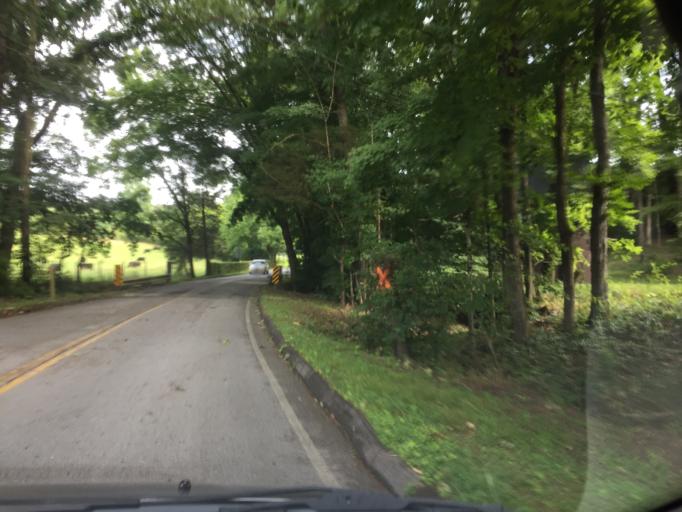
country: US
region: Tennessee
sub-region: Hamilton County
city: Collegedale
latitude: 35.0284
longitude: -85.0498
